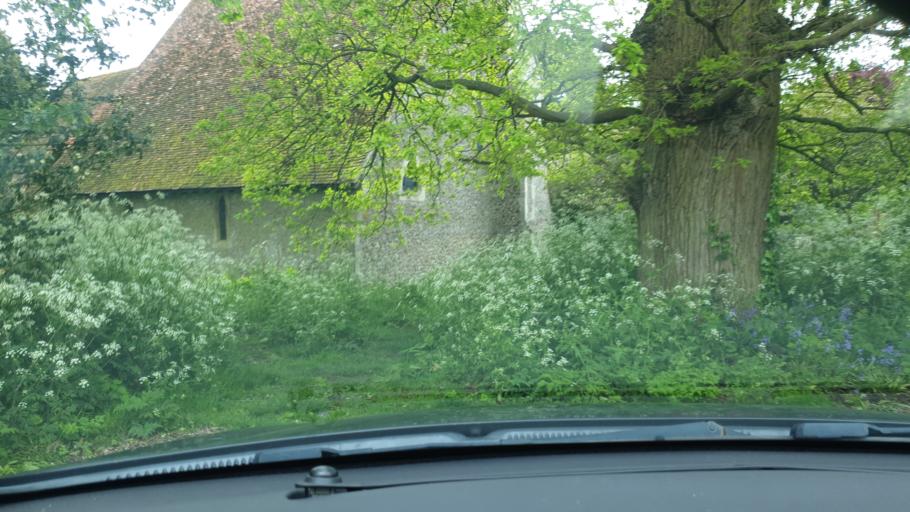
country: GB
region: England
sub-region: Essex
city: Little Clacton
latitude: 51.8779
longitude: 1.1656
